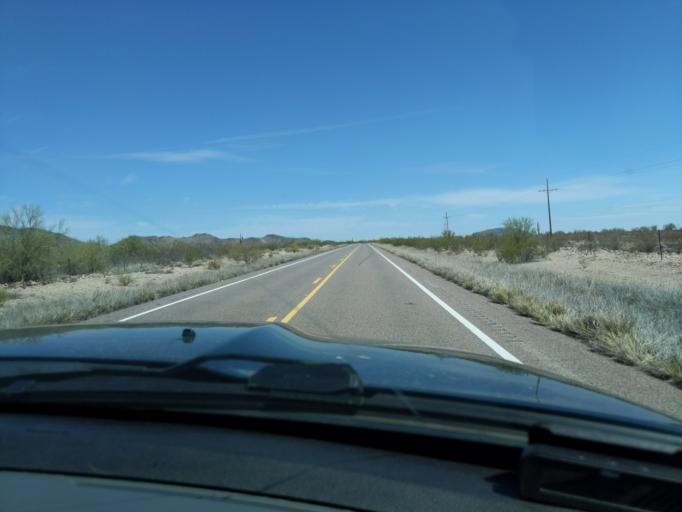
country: US
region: Arizona
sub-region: Pinal County
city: Arizona City
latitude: 32.6361
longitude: -111.8763
